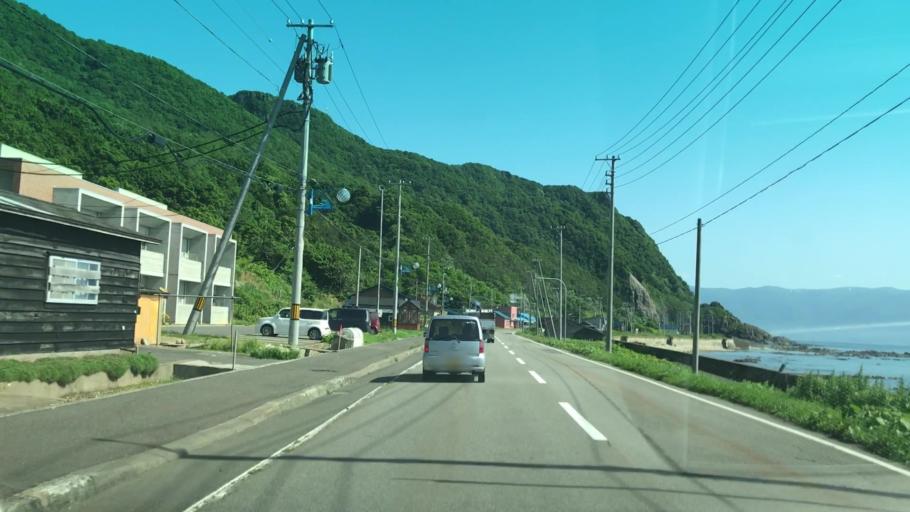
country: JP
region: Hokkaido
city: Iwanai
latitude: 43.0965
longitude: 140.4624
